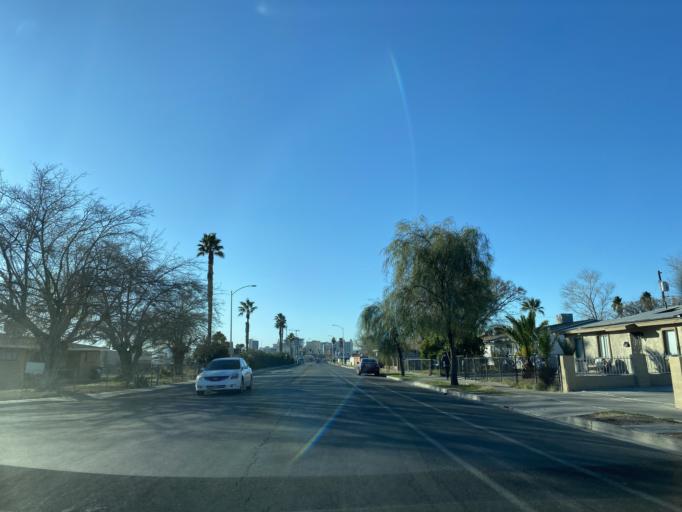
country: US
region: Nevada
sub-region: Clark County
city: Las Vegas
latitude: 36.1911
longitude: -115.1474
